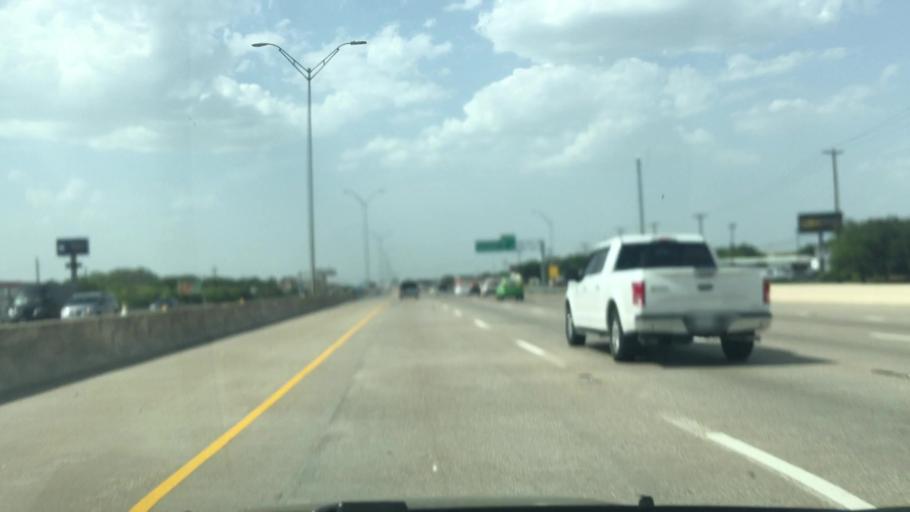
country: US
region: Texas
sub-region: Dallas County
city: DeSoto
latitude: 32.6188
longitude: -96.8230
